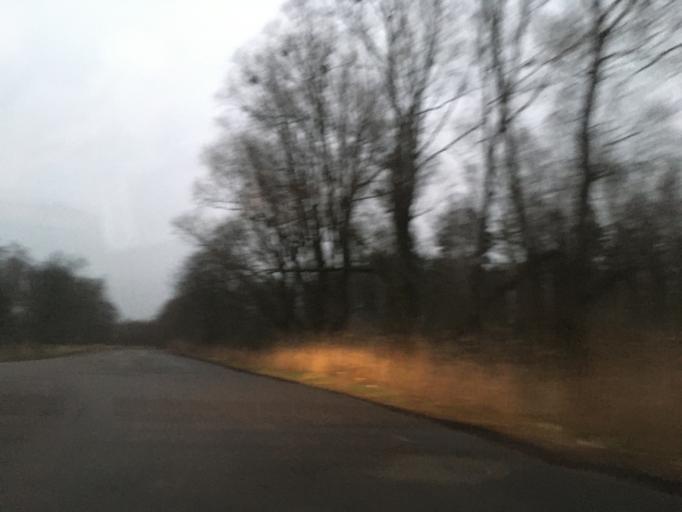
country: PL
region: Warmian-Masurian Voivodeship
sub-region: Powiat elblaski
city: Paslek
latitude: 54.0786
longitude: 19.6131
